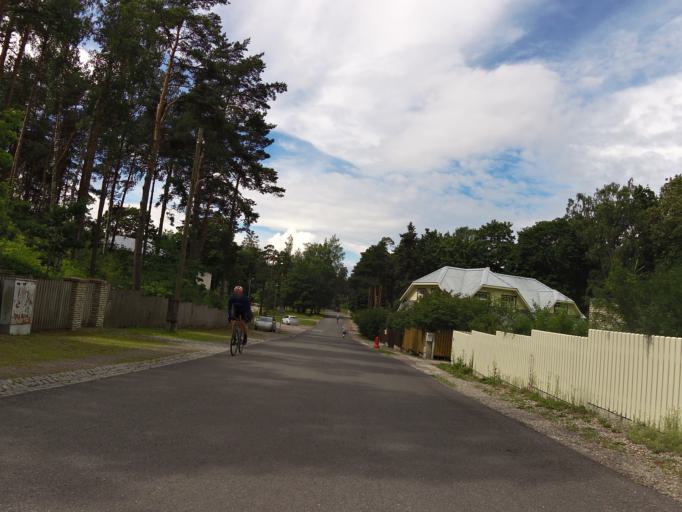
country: EE
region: Harju
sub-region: Saue vald
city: Laagri
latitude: 59.3881
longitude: 24.6633
